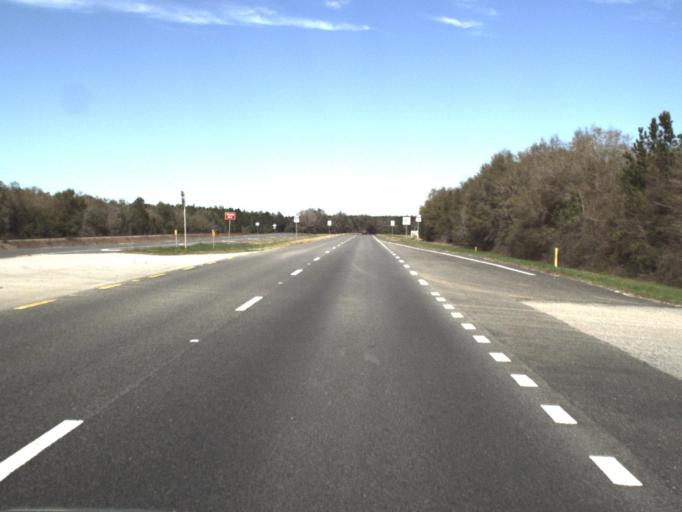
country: US
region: Florida
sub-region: Washington County
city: Chipley
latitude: 30.5988
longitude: -85.3966
